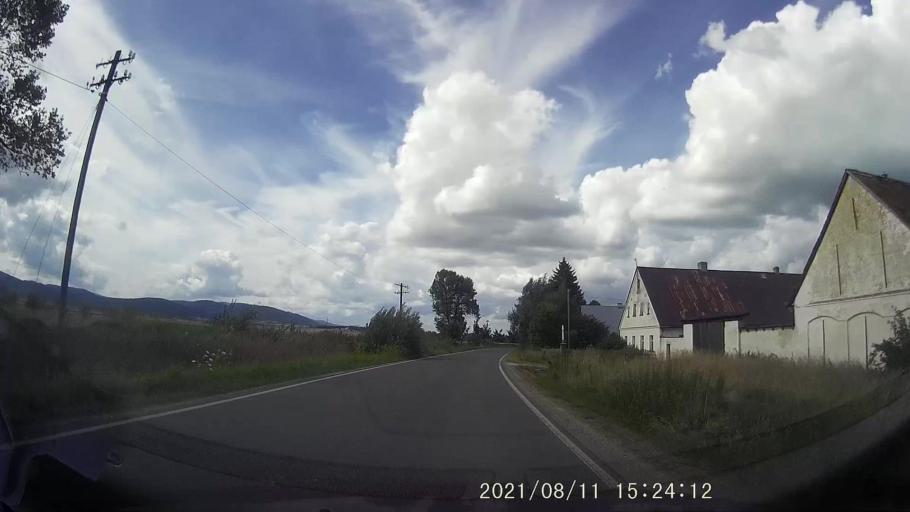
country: PL
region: Lower Silesian Voivodeship
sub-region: Powiat klodzki
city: Bystrzyca Klodzka
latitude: 50.2767
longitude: 16.6852
